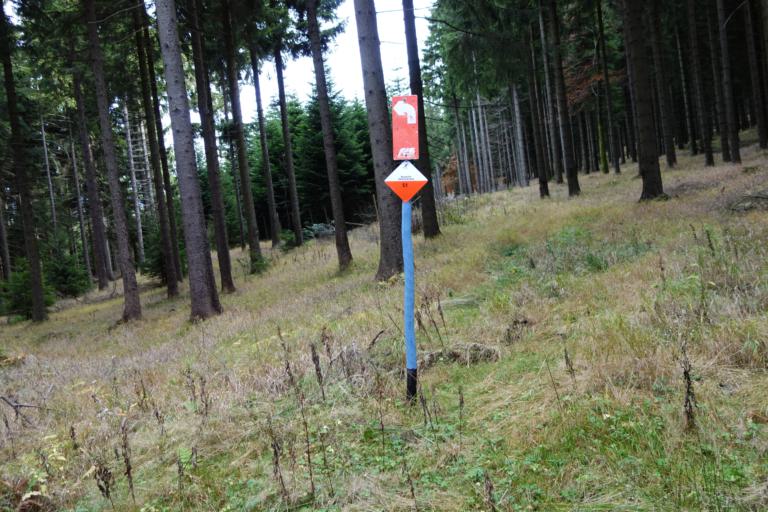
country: DE
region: Saxony
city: Kurort Oberwiesenthal
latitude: 50.4482
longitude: 12.9855
